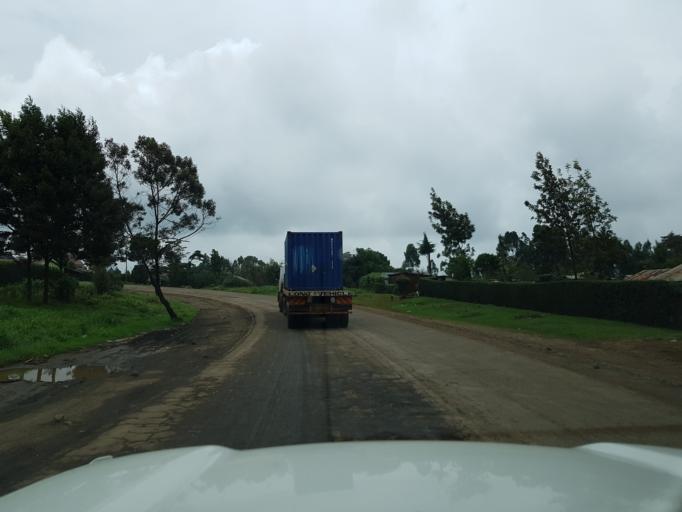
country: KE
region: Kiambu
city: Limuru
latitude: -1.1315
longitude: 36.6361
